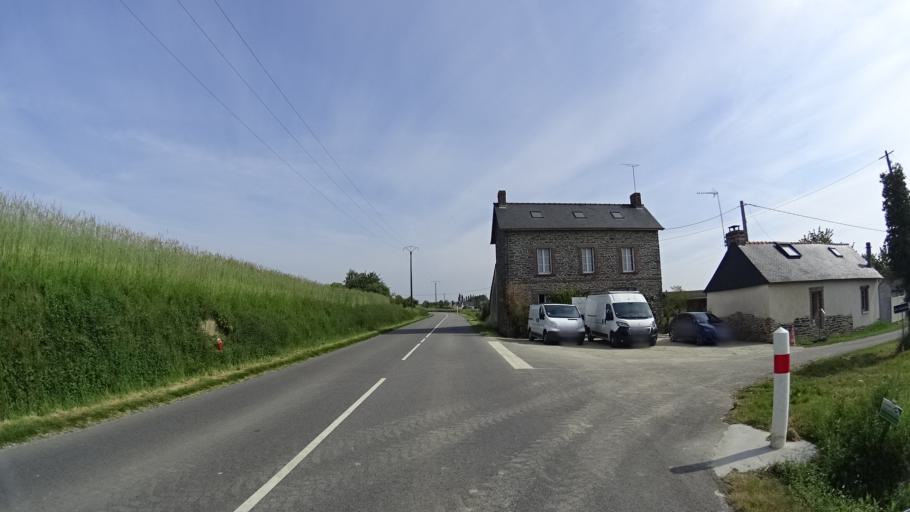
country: FR
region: Brittany
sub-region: Departement d'Ille-et-Vilaine
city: Chateaugiron
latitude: 48.0277
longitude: -1.5056
